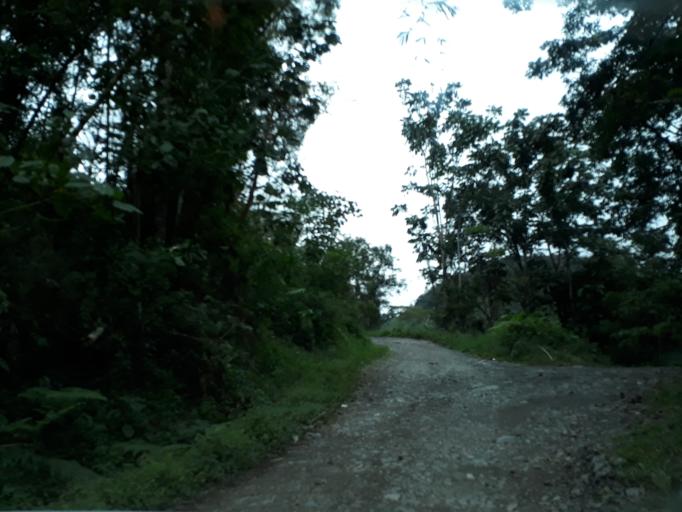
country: CO
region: Boyaca
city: Muzo
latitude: 5.3791
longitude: -74.0859
